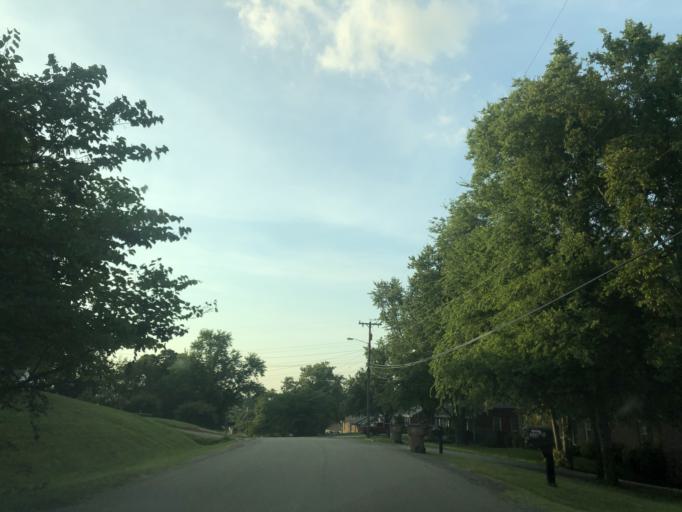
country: US
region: Tennessee
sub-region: Davidson County
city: Nashville
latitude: 36.1609
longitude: -86.7048
